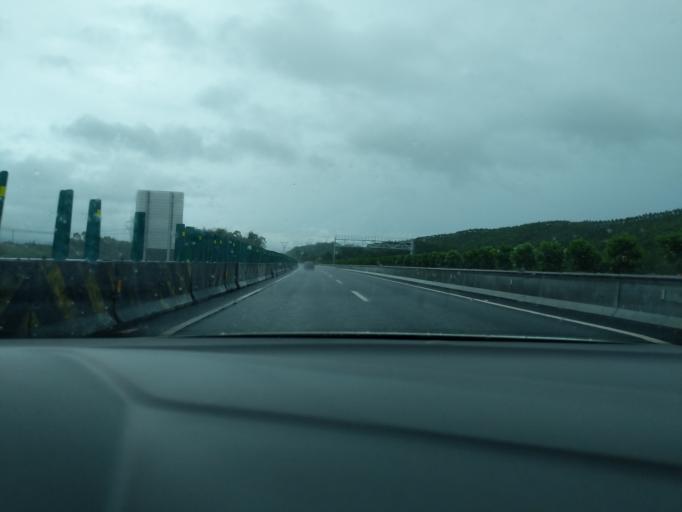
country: CN
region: Guangdong
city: Liangxi
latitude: 22.2735
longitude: 112.3306
